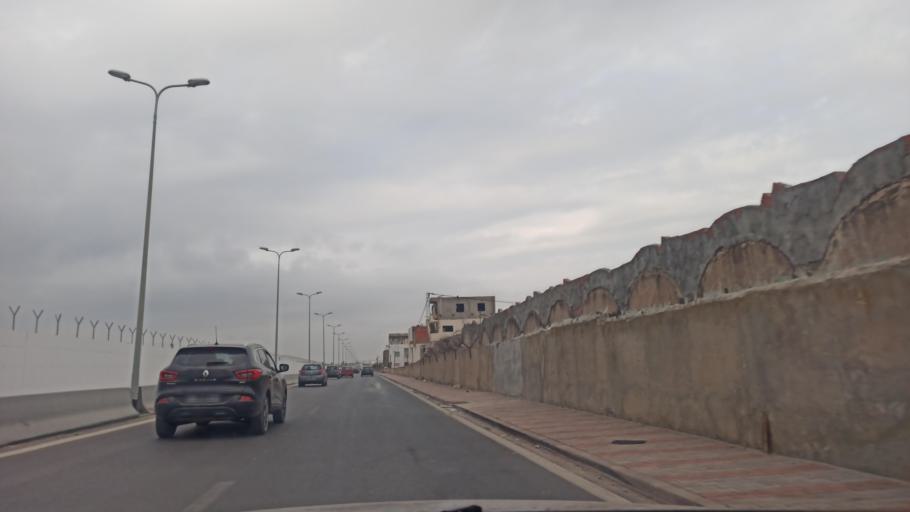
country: TN
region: Ariana
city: Ariana
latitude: 36.8644
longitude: 10.2236
